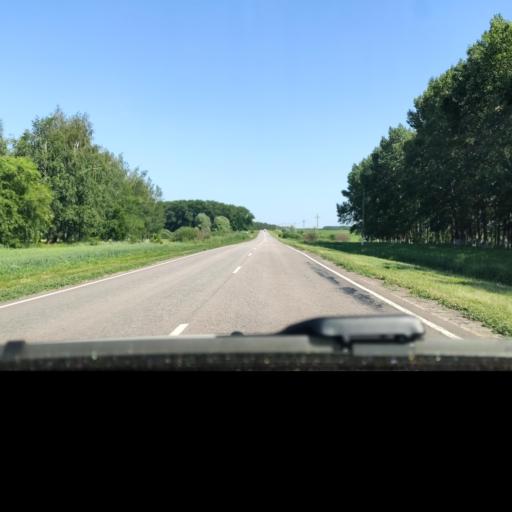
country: RU
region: Voronezj
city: Panino
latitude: 51.6581
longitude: 39.9942
